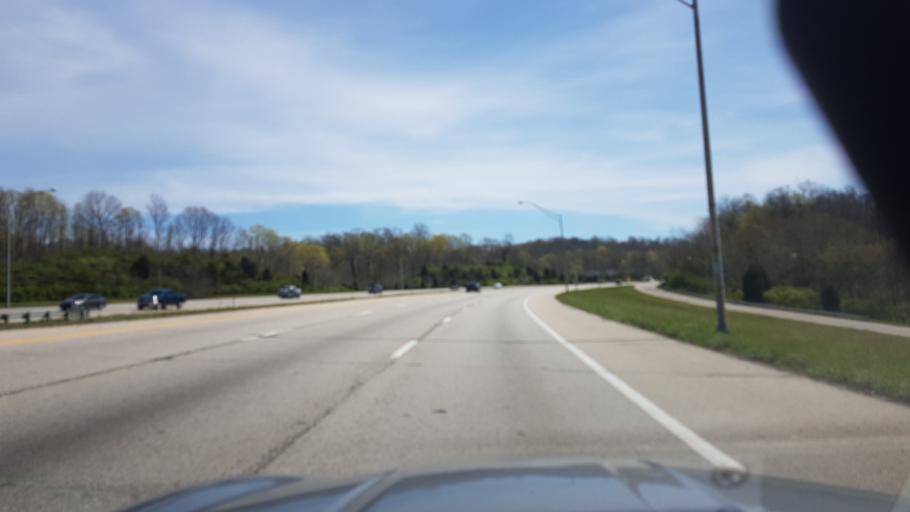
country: US
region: Kentucky
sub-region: Campbell County
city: Fort Thomas
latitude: 39.0604
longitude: -84.4210
